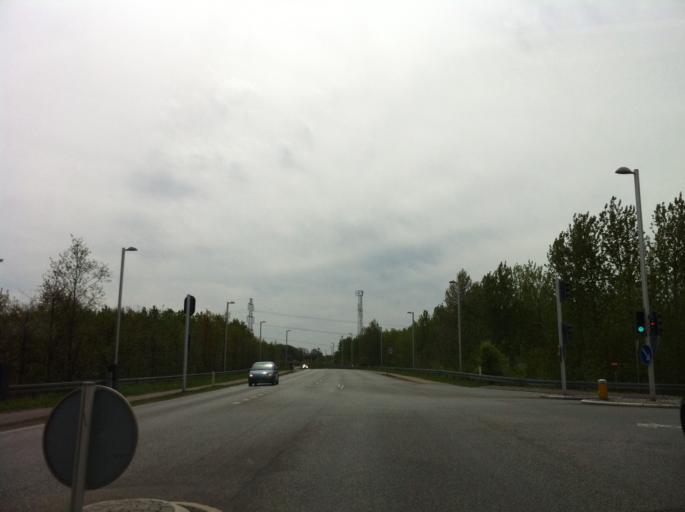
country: DK
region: Zealand
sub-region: Ringsted Kommune
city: Ringsted
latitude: 55.4571
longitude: 11.8258
